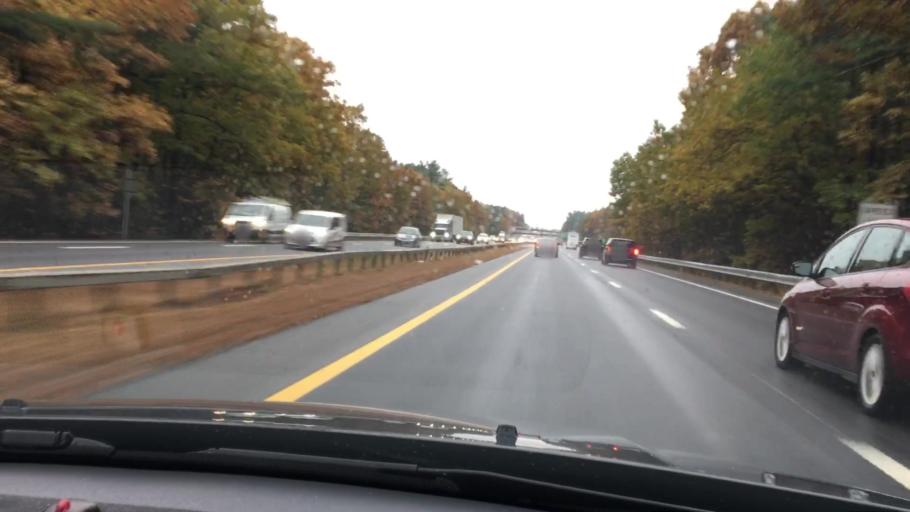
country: US
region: New Hampshire
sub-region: Hillsborough County
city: Nashua
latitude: 42.7986
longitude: -71.4977
